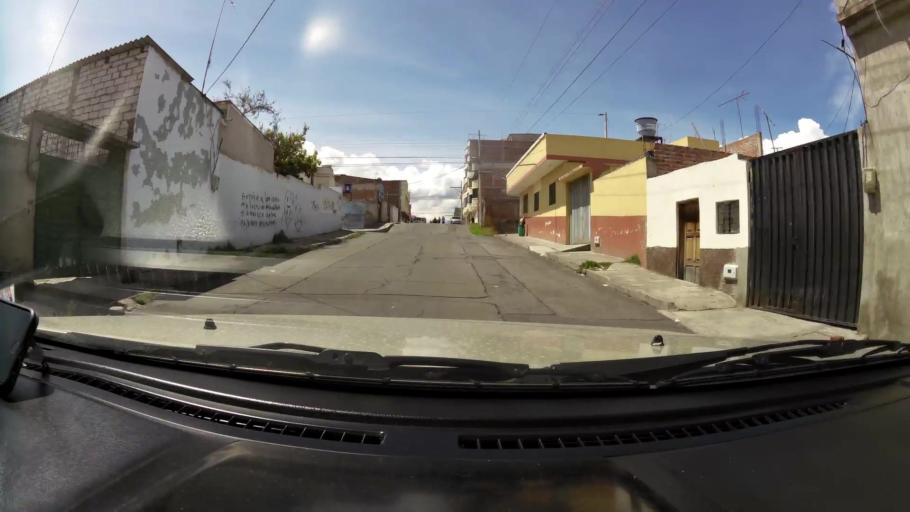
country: EC
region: Chimborazo
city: Riobamba
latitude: -1.6590
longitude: -78.6441
